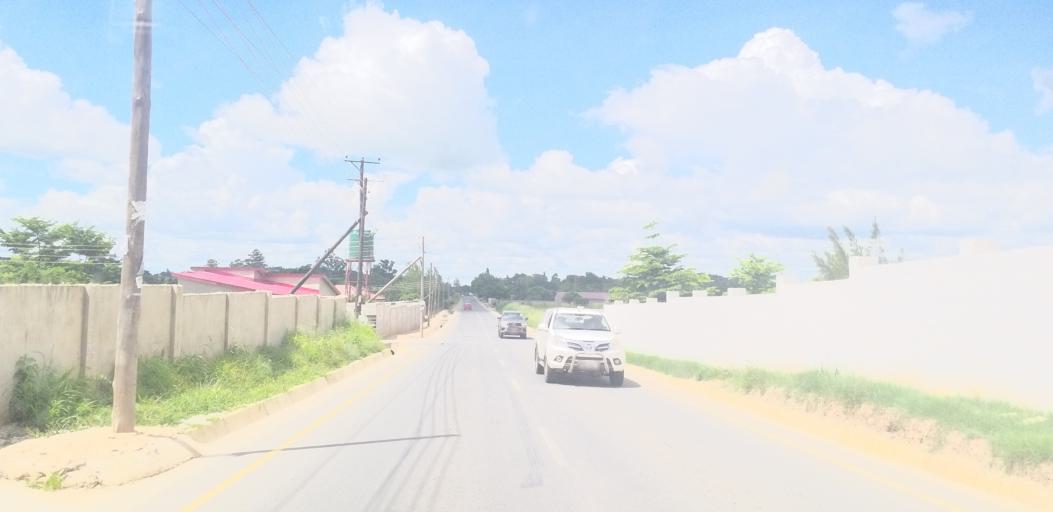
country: ZM
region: Lusaka
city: Lusaka
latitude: -15.3394
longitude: 28.3288
